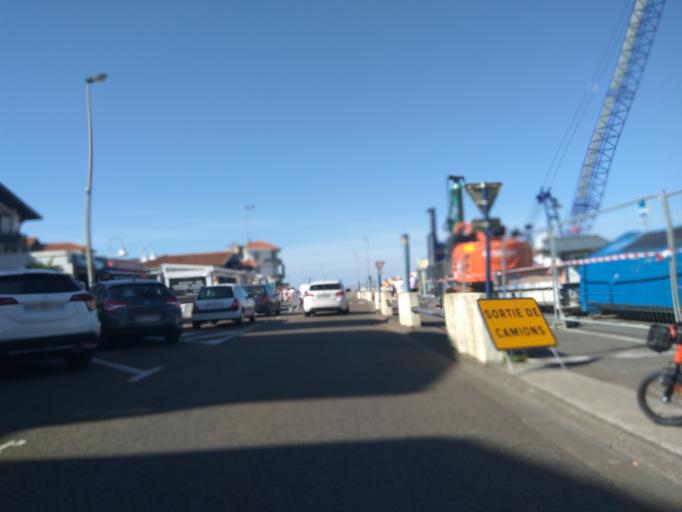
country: FR
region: Aquitaine
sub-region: Departement des Landes
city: Capbreton
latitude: 43.6538
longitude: -1.4409
